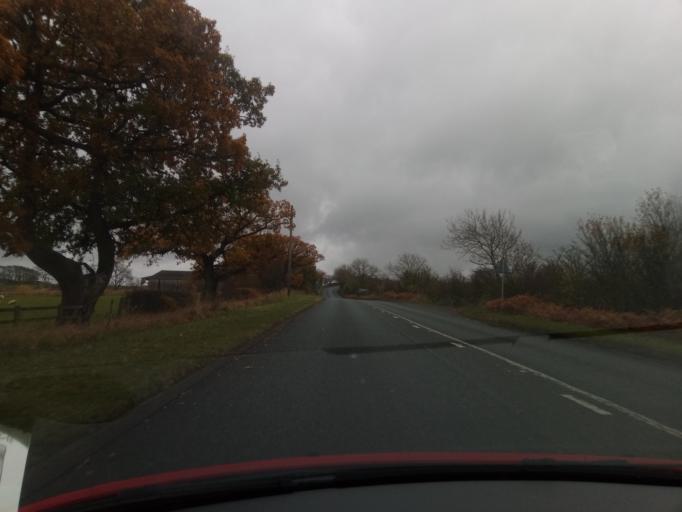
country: GB
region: England
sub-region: County Durham
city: High Etherley
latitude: 54.6558
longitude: -1.7703
